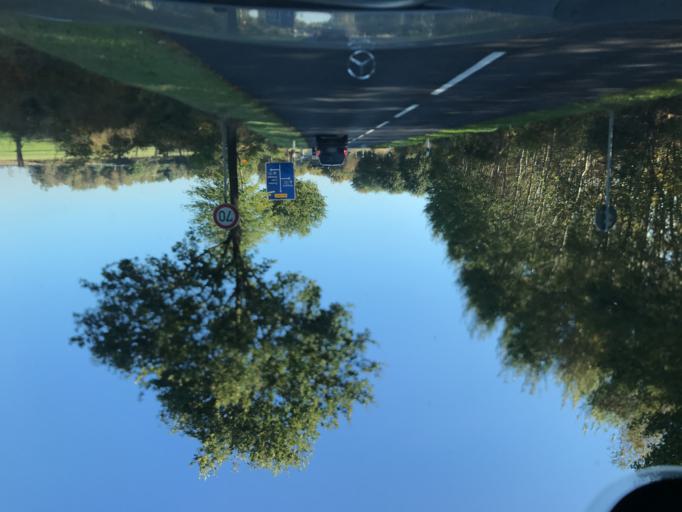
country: DE
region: Lower Saxony
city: Bunde
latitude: 53.1364
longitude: 7.2789
